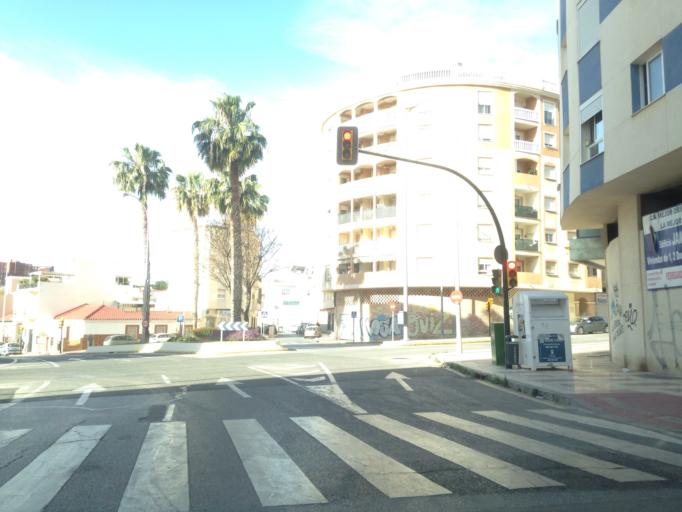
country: ES
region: Andalusia
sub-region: Provincia de Malaga
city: Malaga
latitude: 36.7268
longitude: -4.4385
